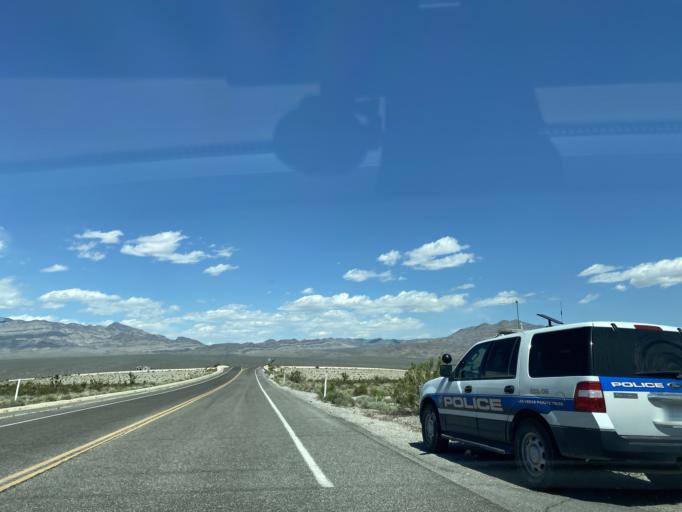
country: US
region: Nevada
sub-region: Clark County
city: Summerlin South
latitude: 36.3589
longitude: -115.3552
